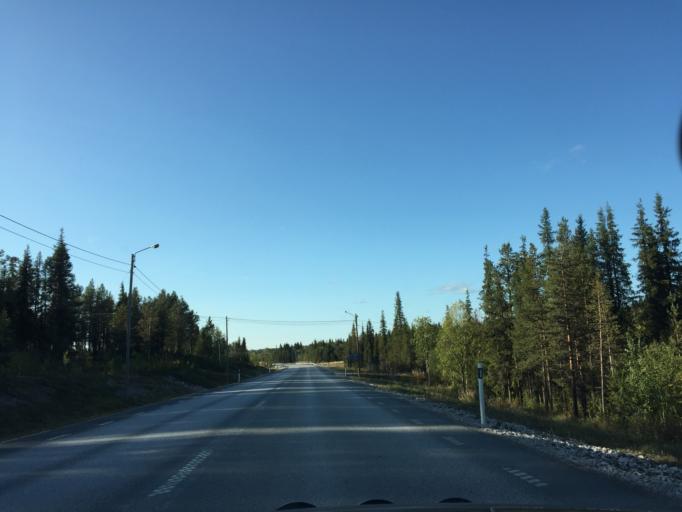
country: SE
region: Norrbotten
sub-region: Gallivare Kommun
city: Malmberget
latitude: 67.6377
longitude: 21.0643
